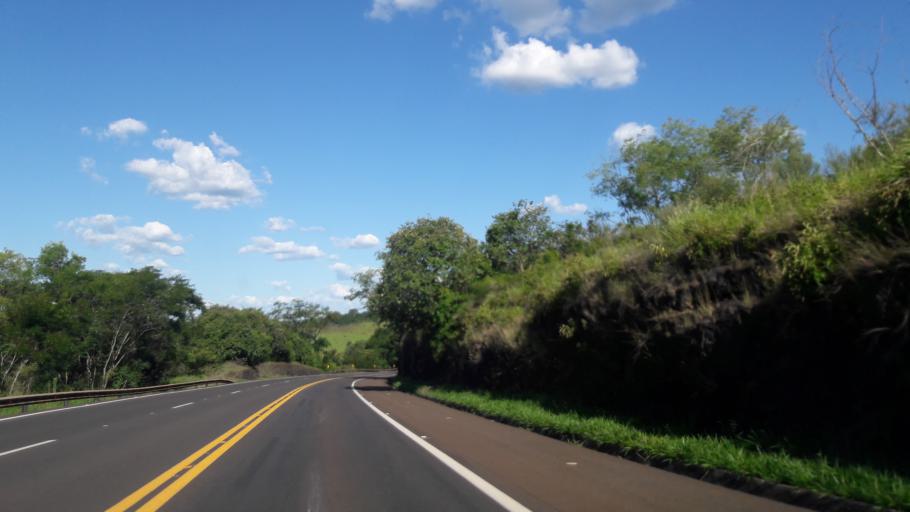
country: BR
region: Parana
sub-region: Laranjeiras Do Sul
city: Laranjeiras do Sul
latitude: -25.4052
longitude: -52.0951
